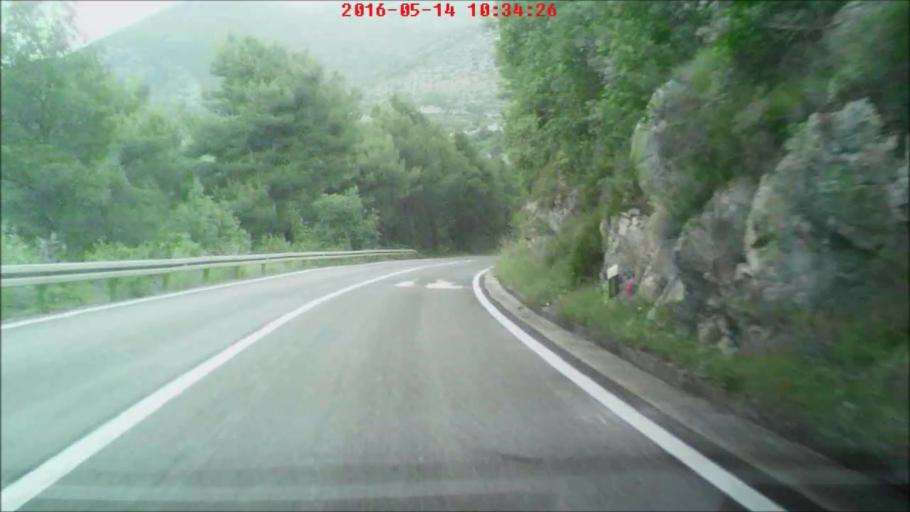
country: HR
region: Dubrovacko-Neretvanska
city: Podgora
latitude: 42.7814
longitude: 17.8905
